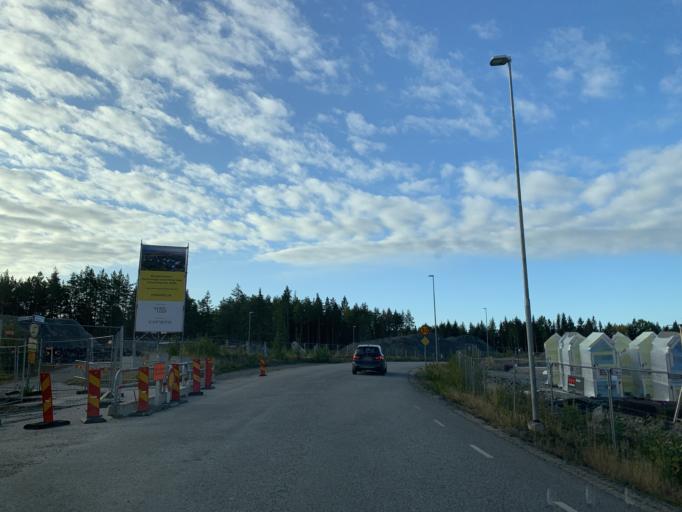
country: SE
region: Stockholm
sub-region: Upplands-Bro Kommun
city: Bro
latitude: 59.5063
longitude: 17.6147
